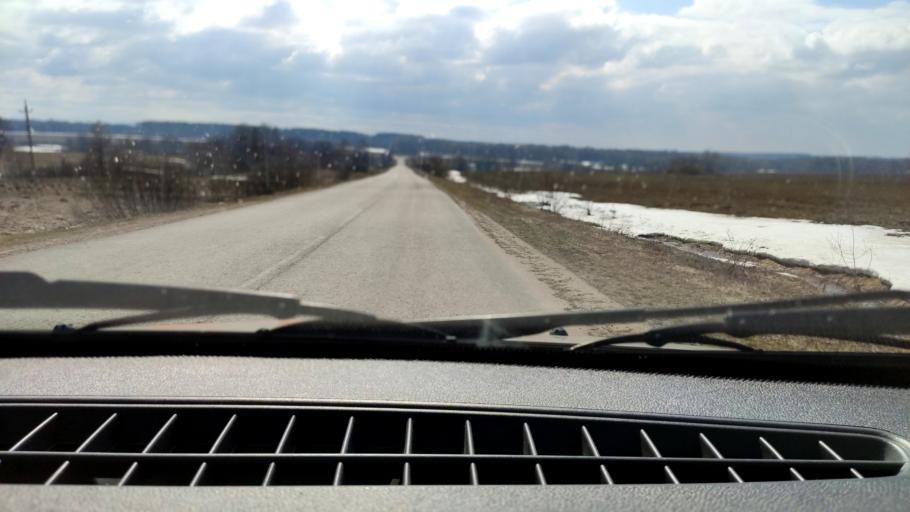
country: RU
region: Bashkortostan
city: Kudeyevskiy
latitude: 54.8250
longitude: 56.7931
